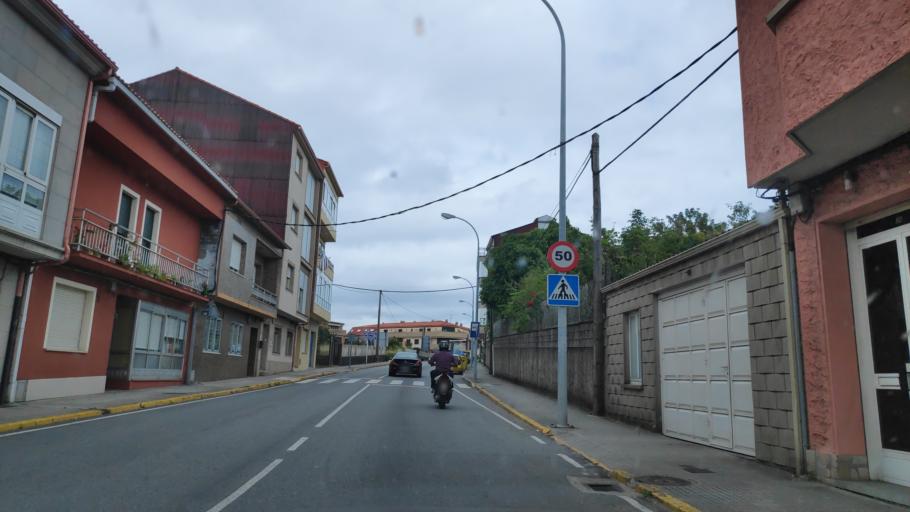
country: ES
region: Galicia
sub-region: Provincia da Coruna
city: Rianxo
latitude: 42.6518
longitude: -8.8155
